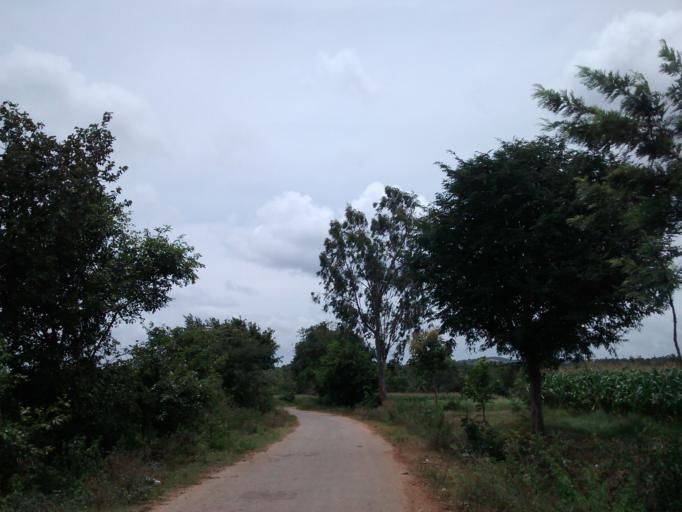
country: IN
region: Karnataka
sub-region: Hassan
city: Hassan
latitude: 12.9171
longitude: 76.1308
